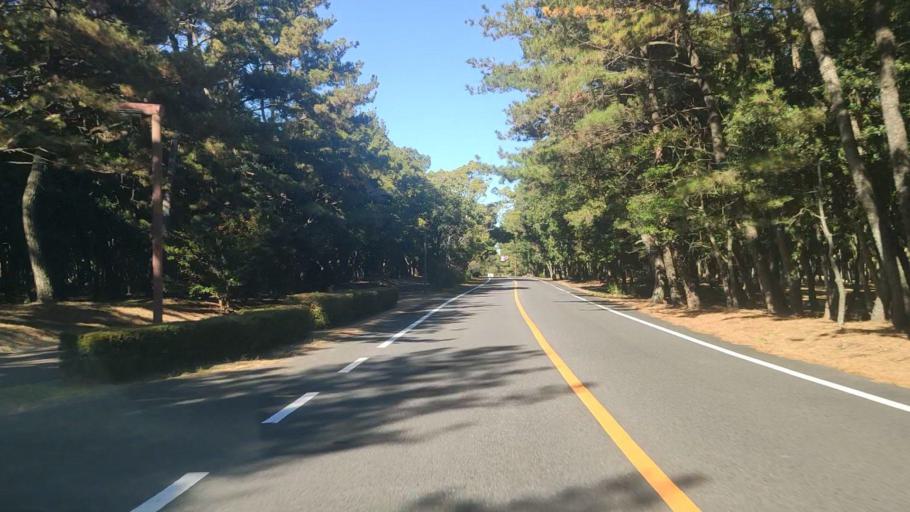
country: JP
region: Miyazaki
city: Miyazaki-shi
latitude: 31.9432
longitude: 131.4648
